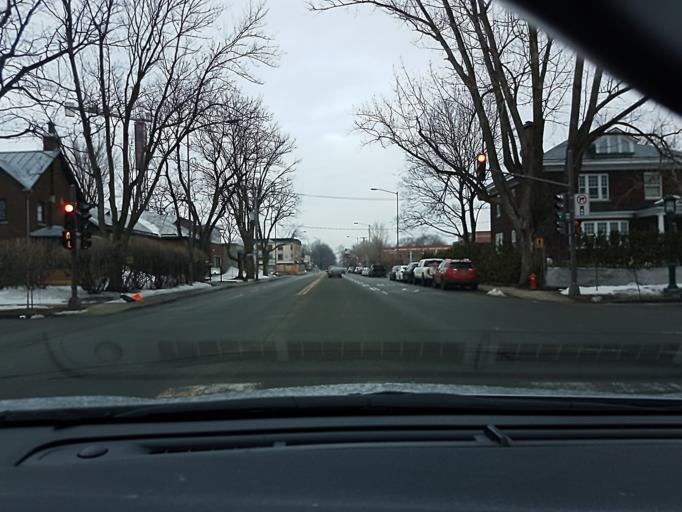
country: CA
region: Quebec
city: Quebec
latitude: 46.7981
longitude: -71.2374
